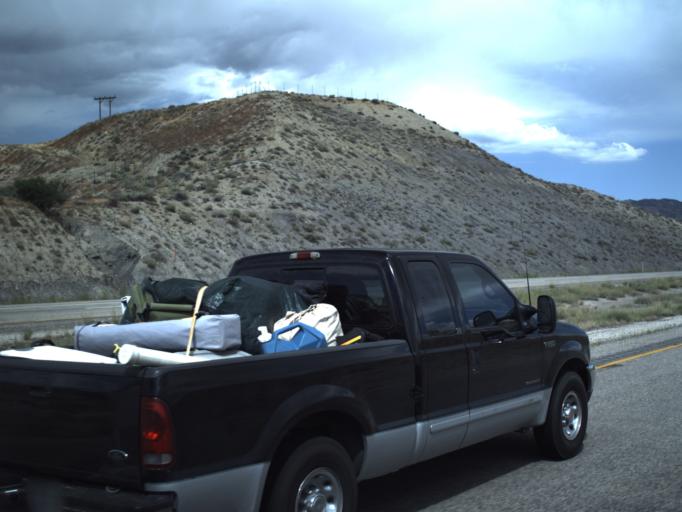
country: US
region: Utah
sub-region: Carbon County
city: Carbonville
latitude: 39.6101
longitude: -110.8346
